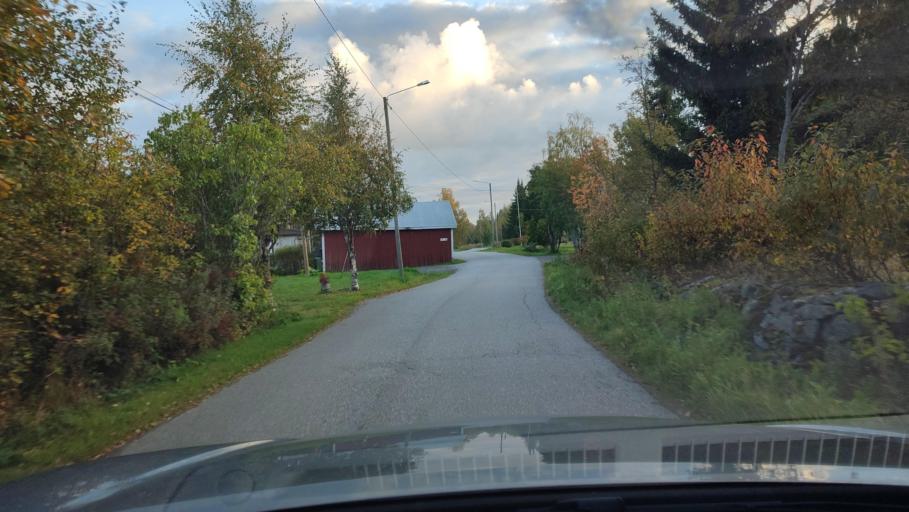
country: FI
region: Ostrobothnia
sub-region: Sydosterbotten
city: Kristinestad
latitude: 62.2455
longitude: 21.5163
